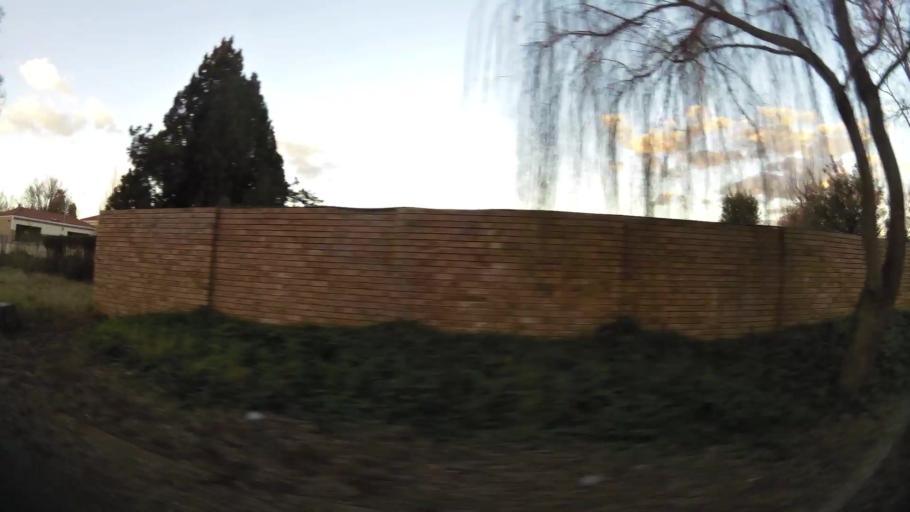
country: ZA
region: North-West
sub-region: Dr Kenneth Kaunda District Municipality
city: Potchefstroom
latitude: -26.7246
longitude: 27.1120
